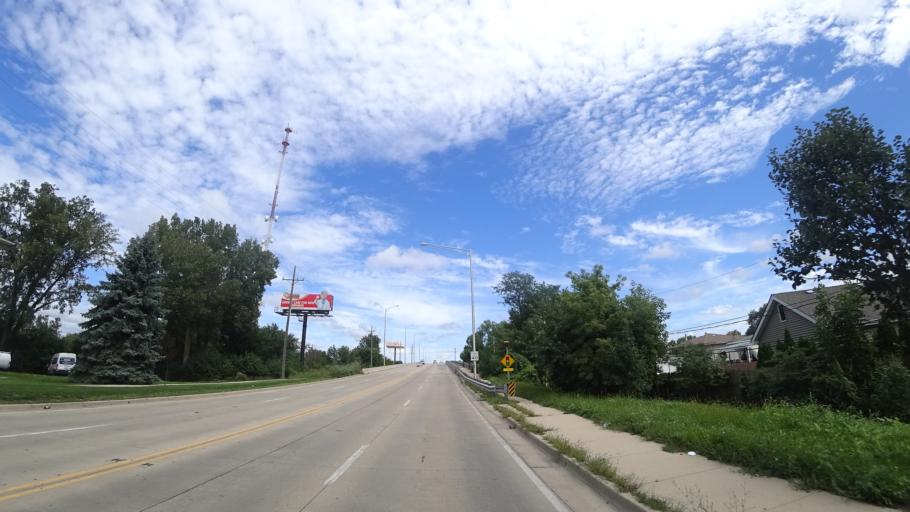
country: US
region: Illinois
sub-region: Cook County
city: Chicago Ridge
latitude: 41.7065
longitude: -87.7844
